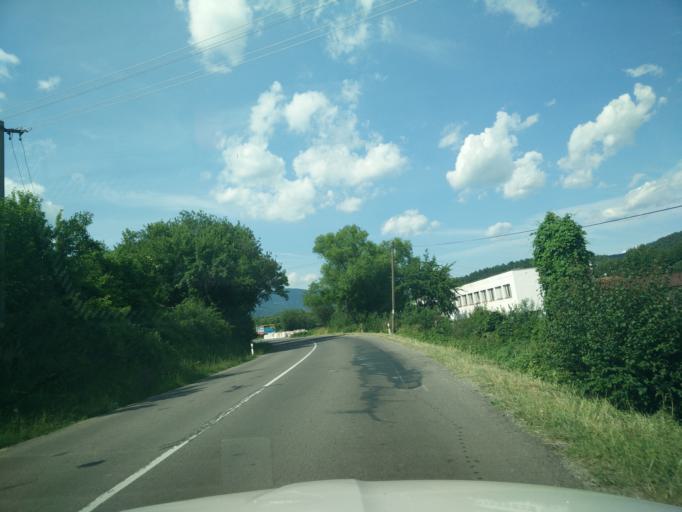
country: SK
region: Nitriansky
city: Prievidza
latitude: 48.8811
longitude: 18.6381
